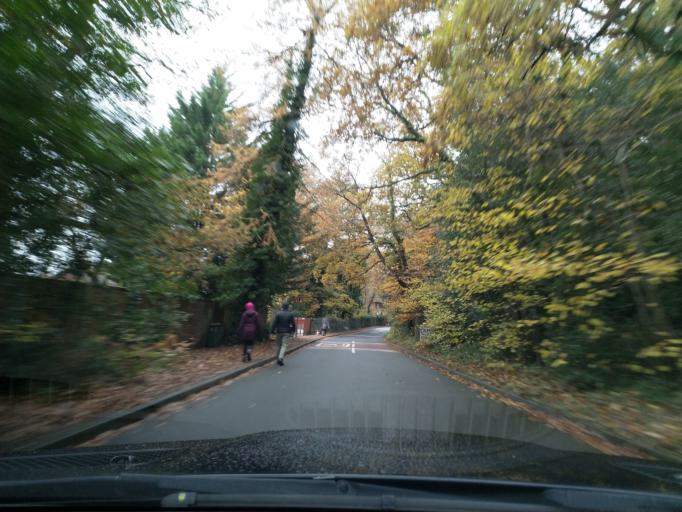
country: GB
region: England
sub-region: Surrey
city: Frimley
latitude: 51.3127
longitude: -0.7224
